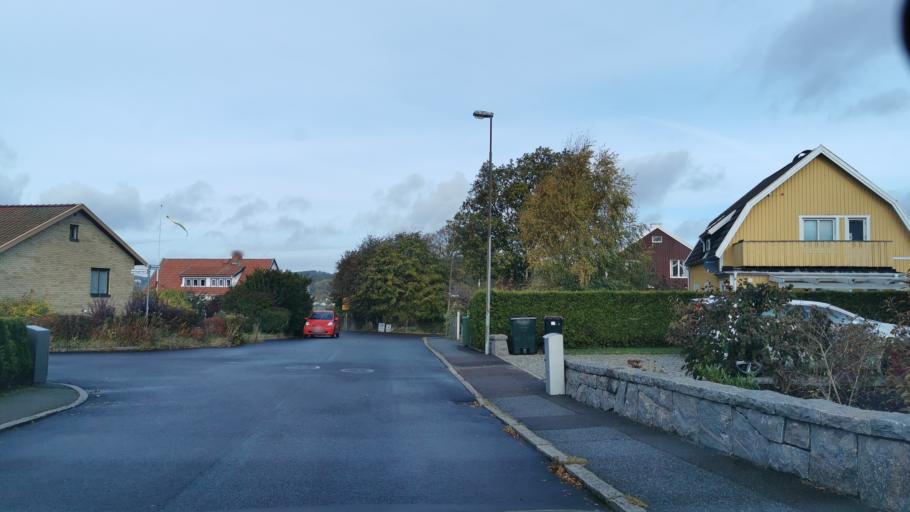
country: SE
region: Vaestra Goetaland
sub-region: Partille Kommun
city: Partille
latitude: 57.7302
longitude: 12.0791
